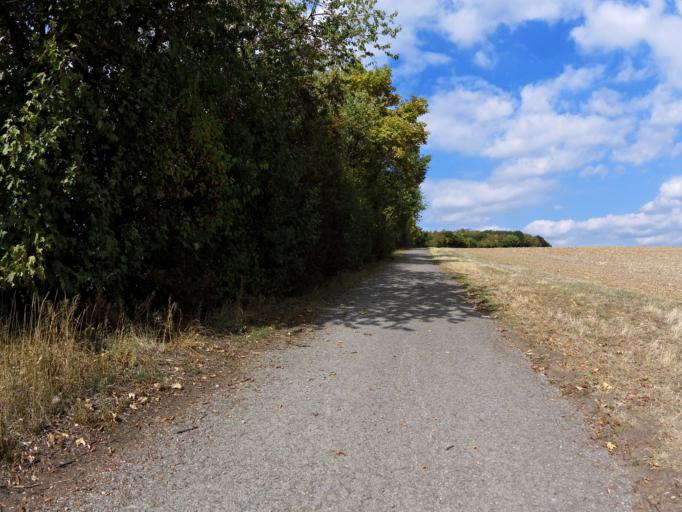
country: DE
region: Bavaria
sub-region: Regierungsbezirk Unterfranken
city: Hettstadt
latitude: 49.7862
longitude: 9.8199
